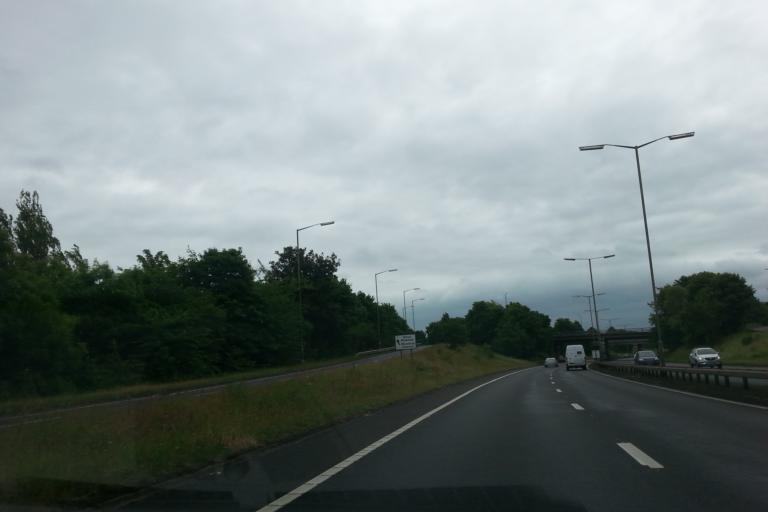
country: GB
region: England
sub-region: Peterborough
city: Peterborough
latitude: 52.5534
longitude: -0.2696
